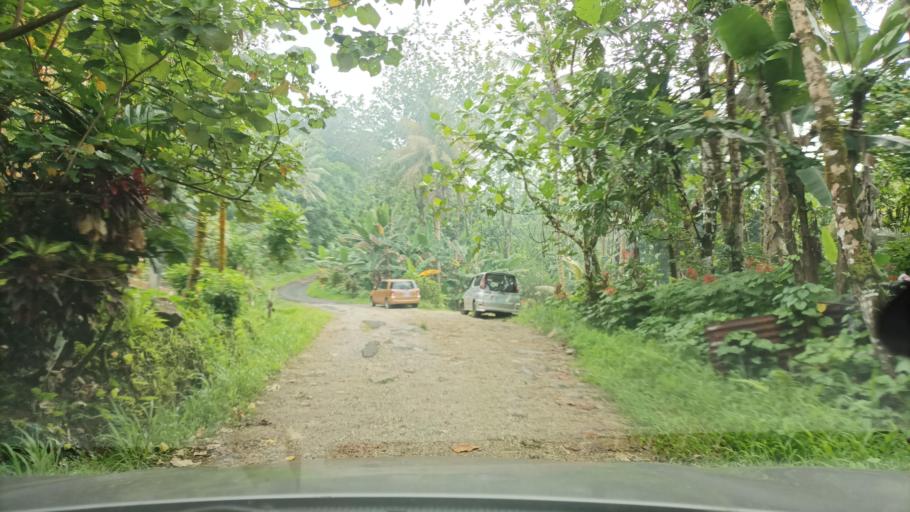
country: FM
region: Pohnpei
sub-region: Kolonia Municipality
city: Kolonia
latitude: 6.9413
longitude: 158.2746
